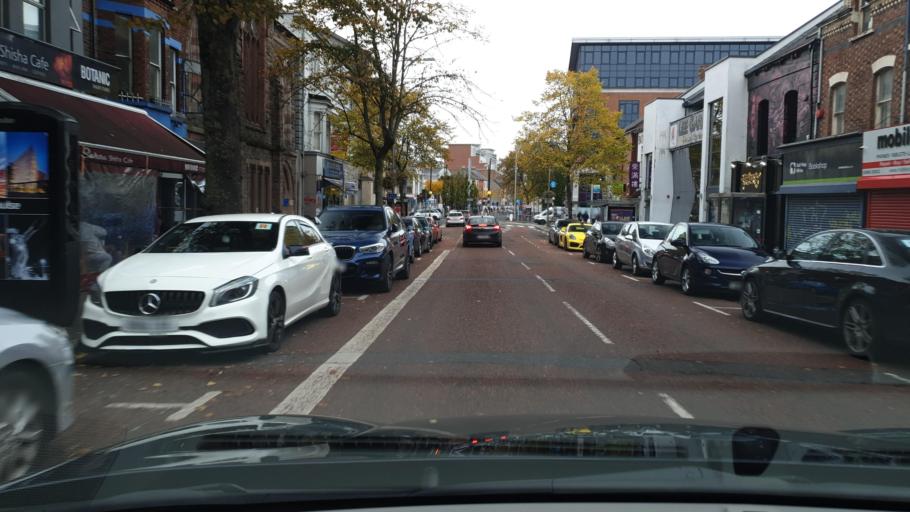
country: GB
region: Northern Ireland
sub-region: City of Belfast
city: Belfast
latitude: 54.5887
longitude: -5.9334
